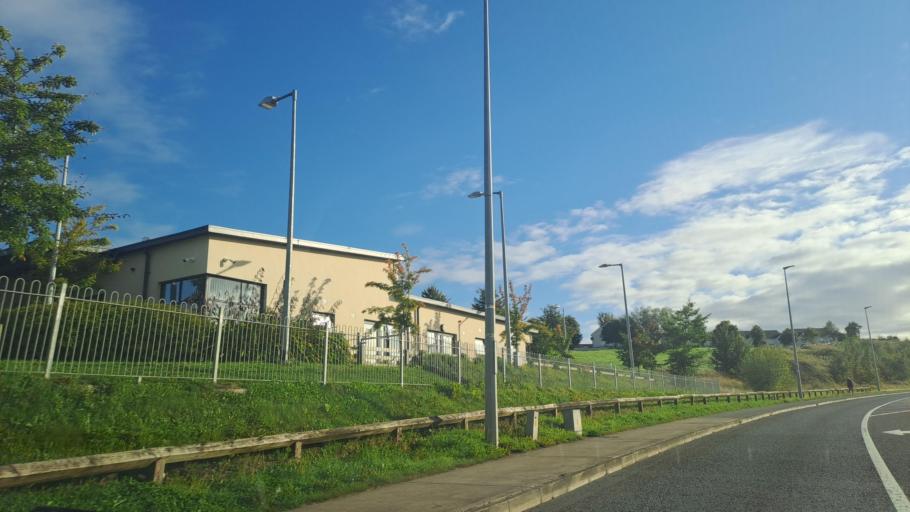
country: IE
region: Ulster
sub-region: County Monaghan
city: Carrickmacross
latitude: 53.9694
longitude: -6.7101
